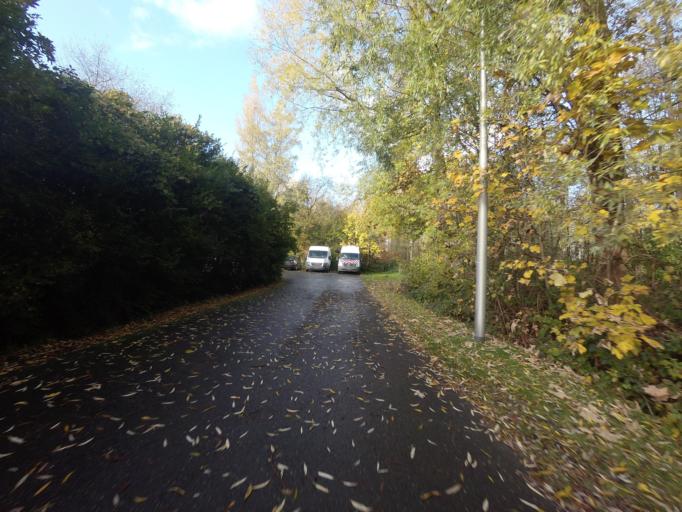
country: BE
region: Flanders
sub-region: Provincie Antwerpen
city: Niel
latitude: 51.1029
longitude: 4.3354
